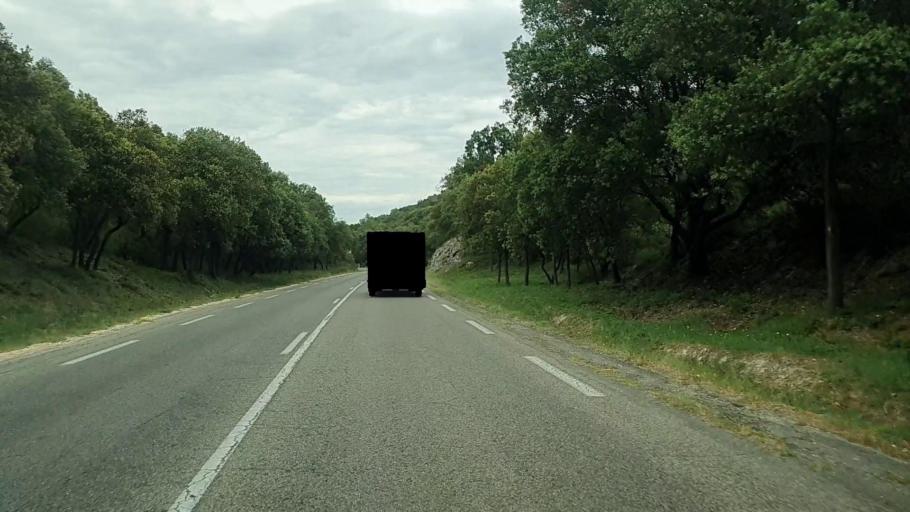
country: FR
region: Languedoc-Roussillon
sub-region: Departement du Gard
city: Connaux
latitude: 44.0693
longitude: 4.5795
